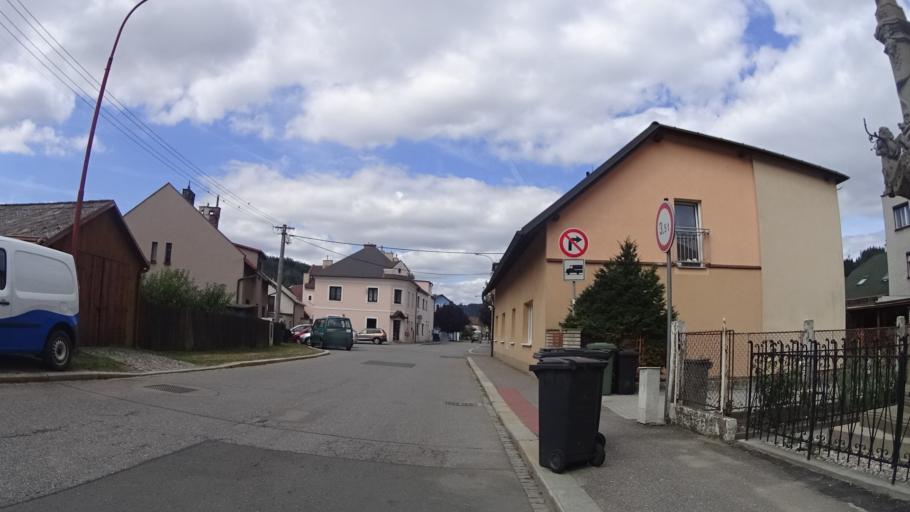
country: CZ
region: Pardubicky
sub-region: Okres Usti nad Orlici
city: Usti nad Orlici
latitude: 49.9697
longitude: 16.3712
